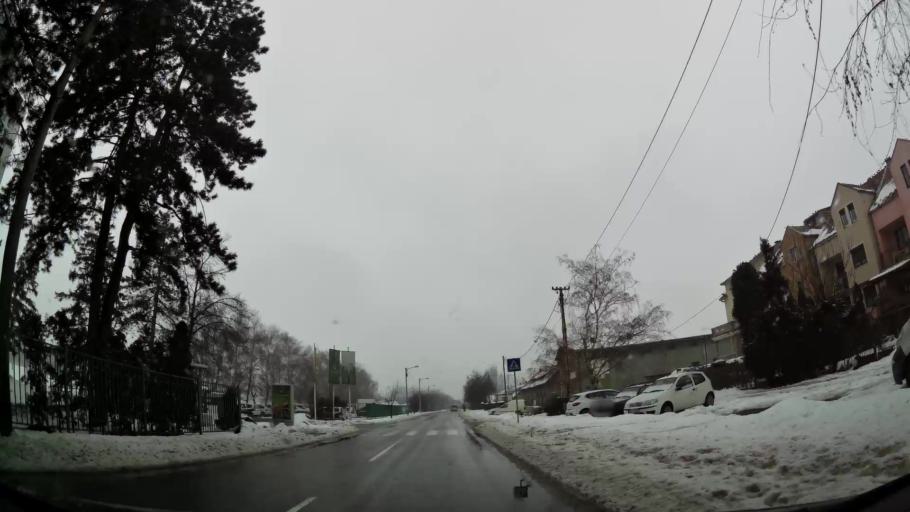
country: RS
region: Central Serbia
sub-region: Belgrade
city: Zemun
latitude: 44.8698
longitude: 20.3286
